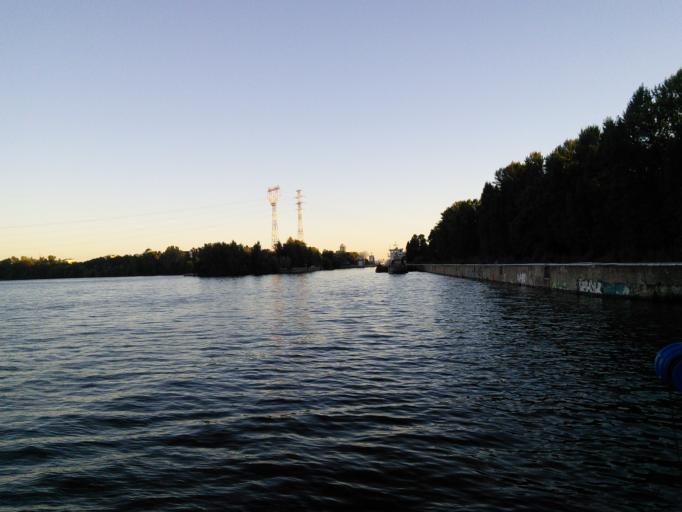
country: RU
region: Moskovskaya
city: Levoberezhnyy
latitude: 55.8408
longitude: 37.4679
